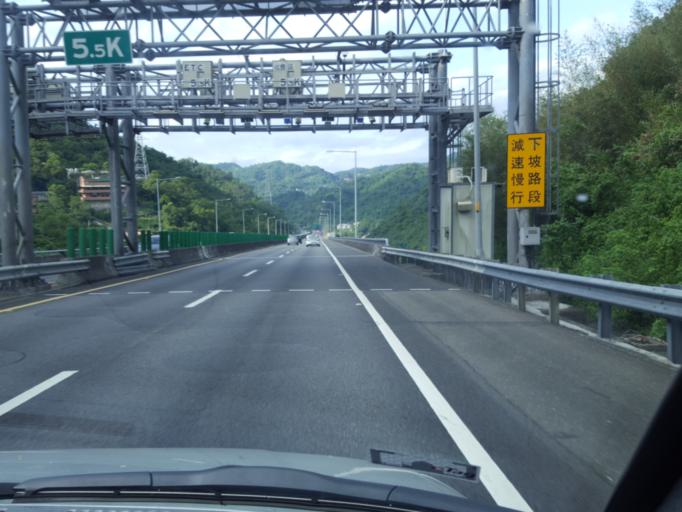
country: TW
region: Taipei
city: Taipei
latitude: 24.9961
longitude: 121.6522
